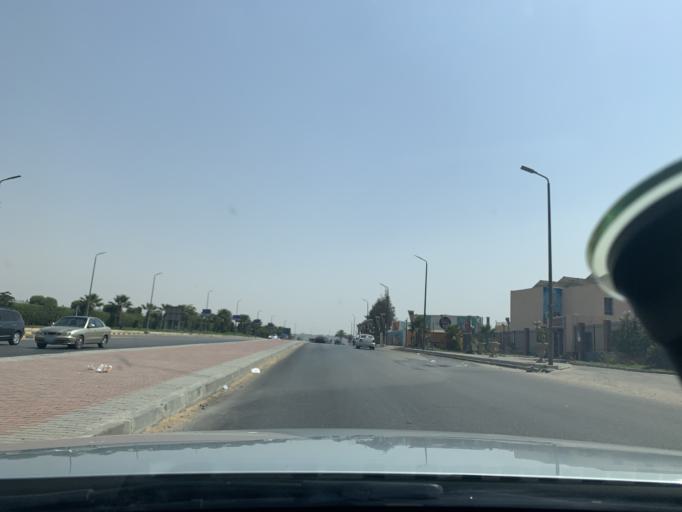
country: EG
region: Muhafazat al Qalyubiyah
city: Al Khankah
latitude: 30.0954
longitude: 31.3827
